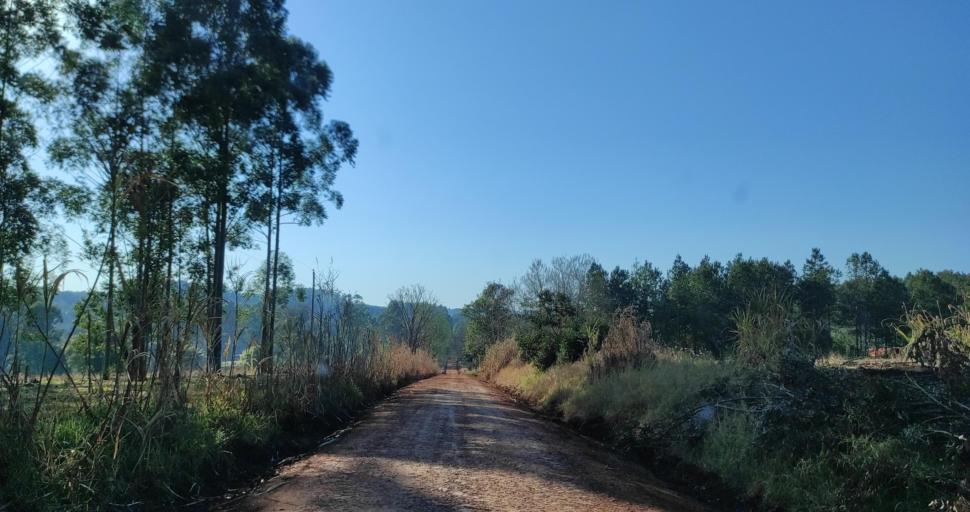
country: AR
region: Misiones
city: Capiovi
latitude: -26.8801
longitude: -55.0356
